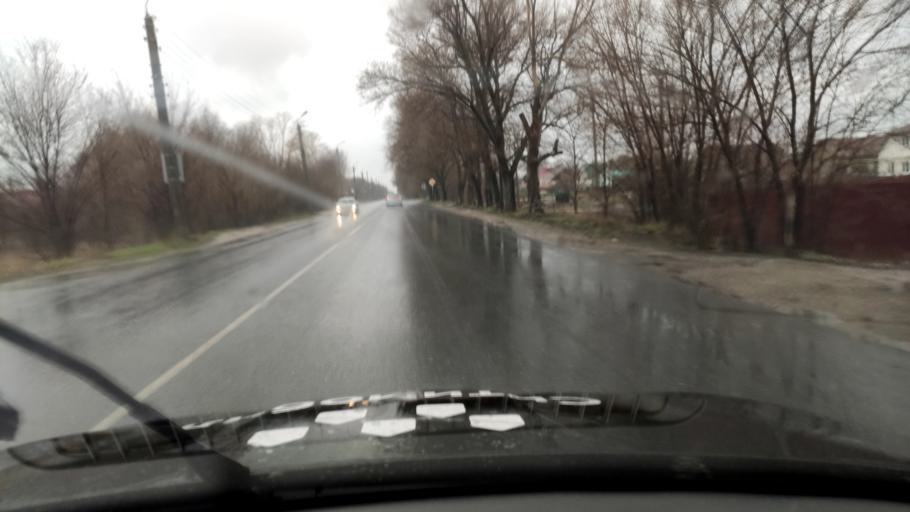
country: RU
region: Samara
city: Varlamovo
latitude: 53.1849
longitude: 48.3832
